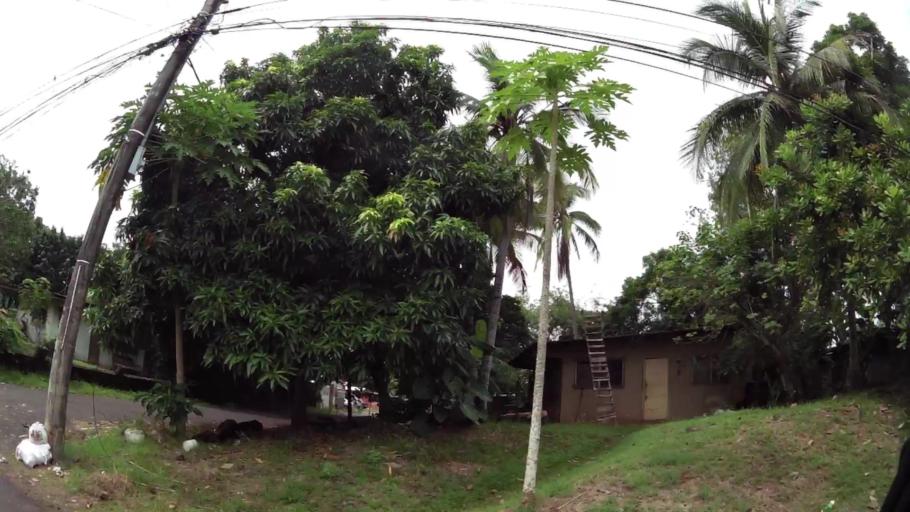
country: PA
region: Panama
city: San Miguelito
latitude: 9.0424
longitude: -79.4324
